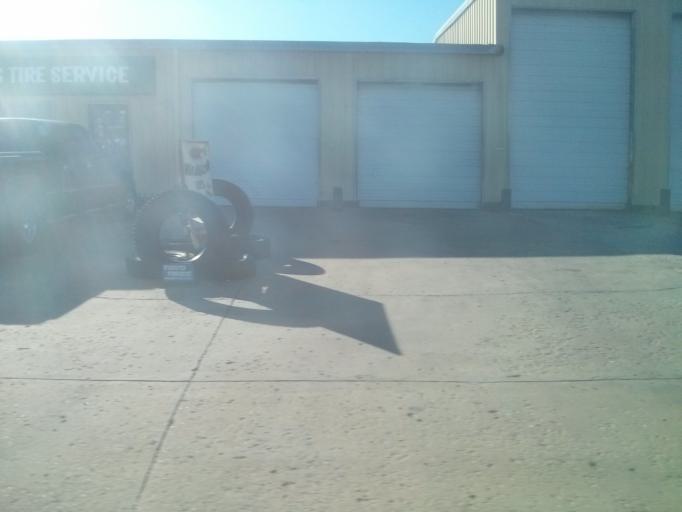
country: US
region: Oklahoma
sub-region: Tulsa County
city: Tulsa
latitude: 36.1770
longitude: -95.9233
